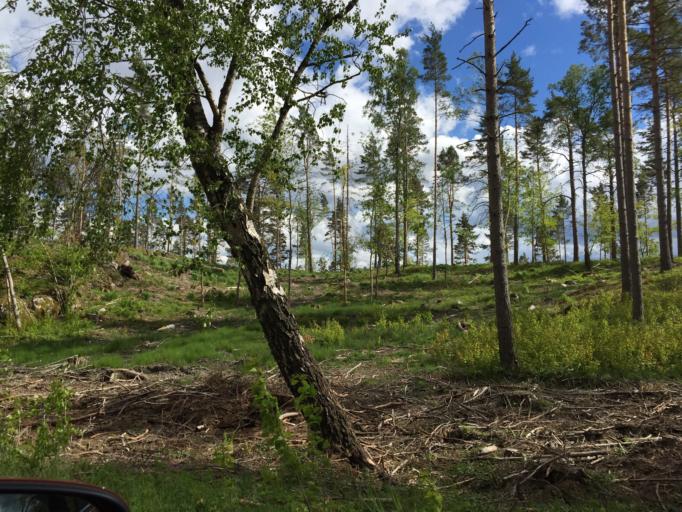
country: SE
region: OEstergoetland
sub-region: Finspangs Kommun
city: Finspang
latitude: 58.7141
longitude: 15.8285
